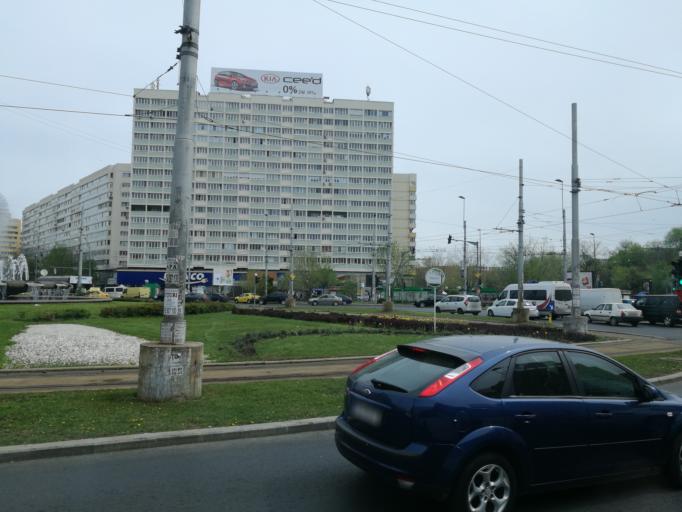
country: RO
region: Bucuresti
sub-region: Municipiul Bucuresti
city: Bucharest
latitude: 44.4492
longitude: 26.1244
